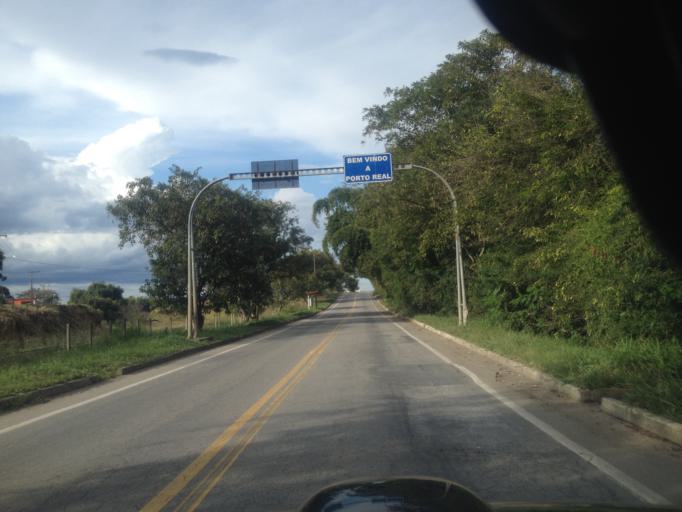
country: BR
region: Rio de Janeiro
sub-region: Porto Real
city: Porto Real
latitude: -22.4466
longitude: -44.3201
